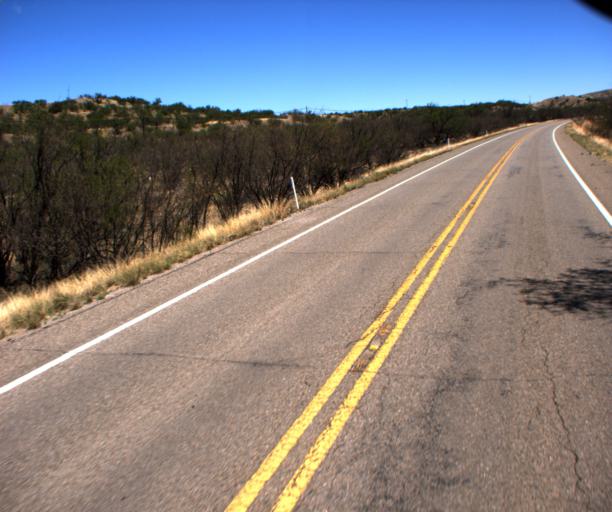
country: US
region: Arizona
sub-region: Santa Cruz County
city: Rio Rico
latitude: 31.6183
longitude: -110.7195
